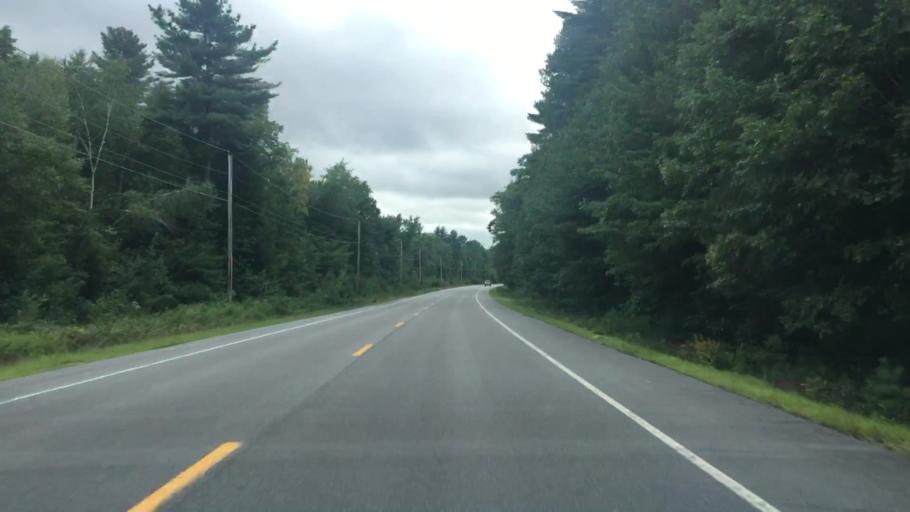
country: US
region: Maine
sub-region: York County
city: Limerick
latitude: 43.7437
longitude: -70.8139
